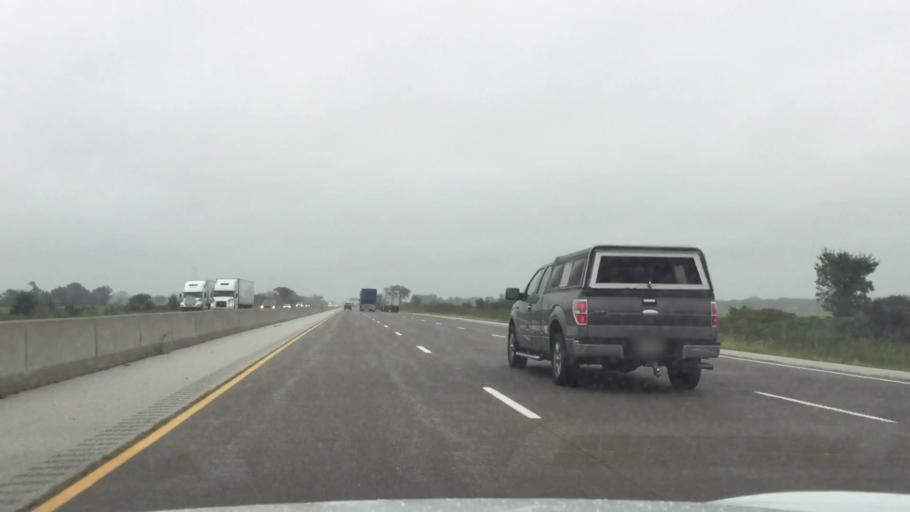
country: US
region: Michigan
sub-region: Wayne County
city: Grosse Pointe
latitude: 42.2368
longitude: -82.7351
